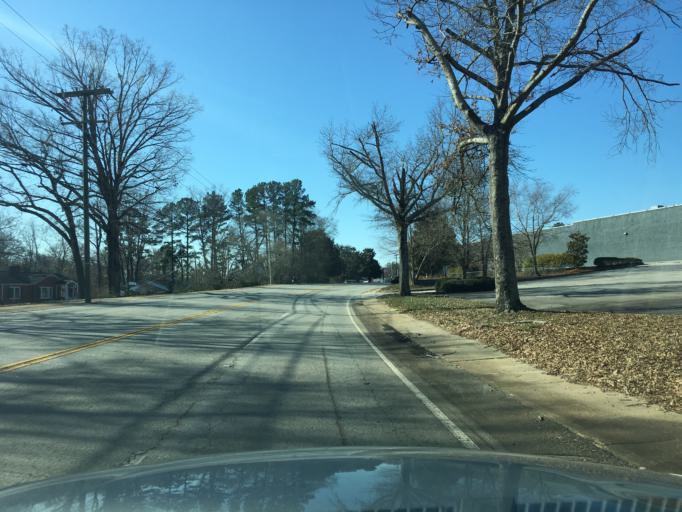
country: US
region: South Carolina
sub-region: Greenville County
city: Berea
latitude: 34.8874
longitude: -82.4543
